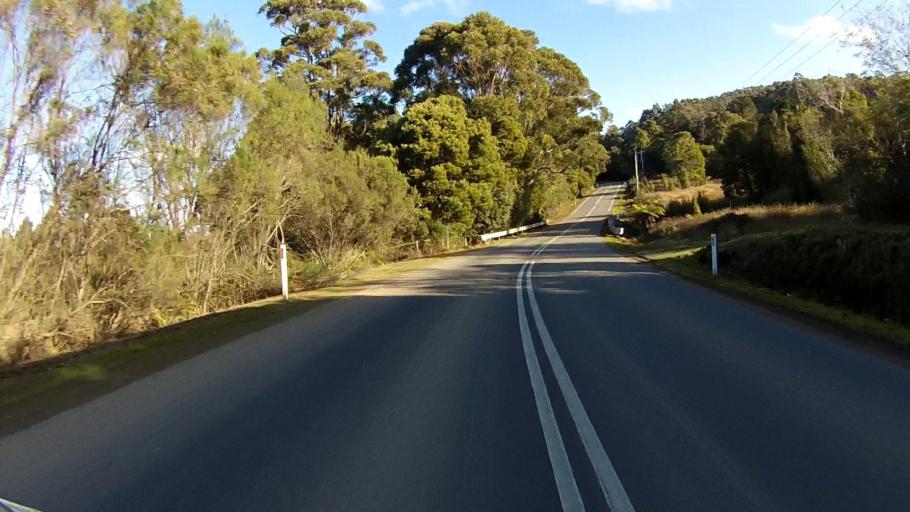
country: AU
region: Tasmania
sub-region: Clarence
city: Sandford
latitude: -43.1117
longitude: 147.8589
